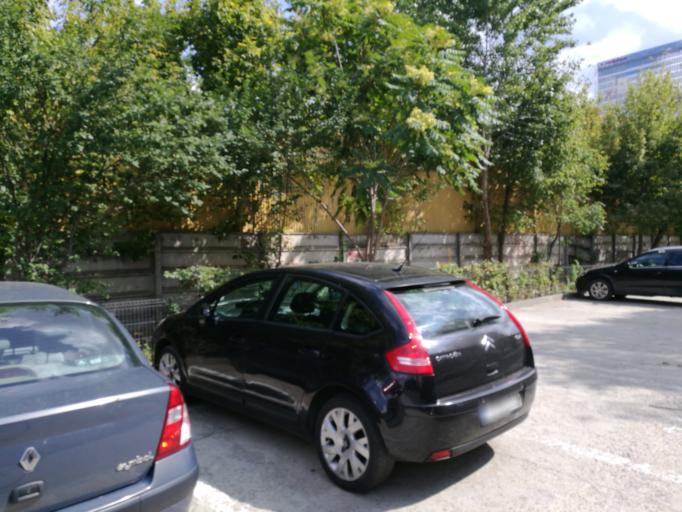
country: RO
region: Bucuresti
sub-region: Municipiul Bucuresti
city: Bucharest
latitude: 44.4827
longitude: 26.1017
